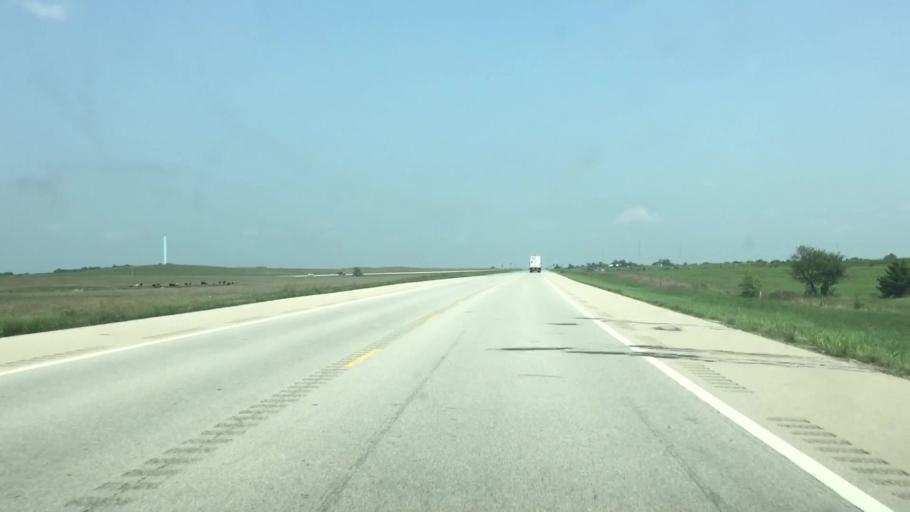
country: US
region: Kansas
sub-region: Allen County
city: Iola
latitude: 38.0763
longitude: -95.3747
